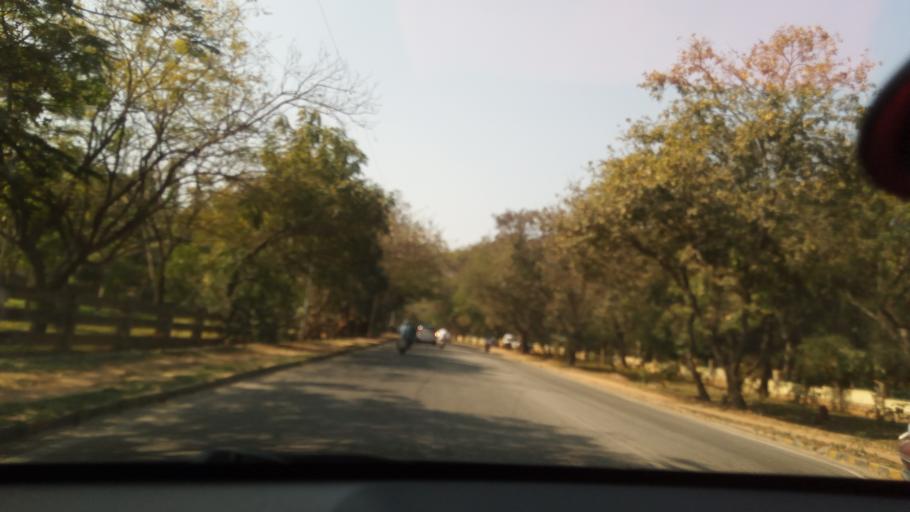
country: IN
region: Karnataka
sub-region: Bangalore Urban
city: Yelahanka
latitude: 13.0475
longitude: 77.5552
